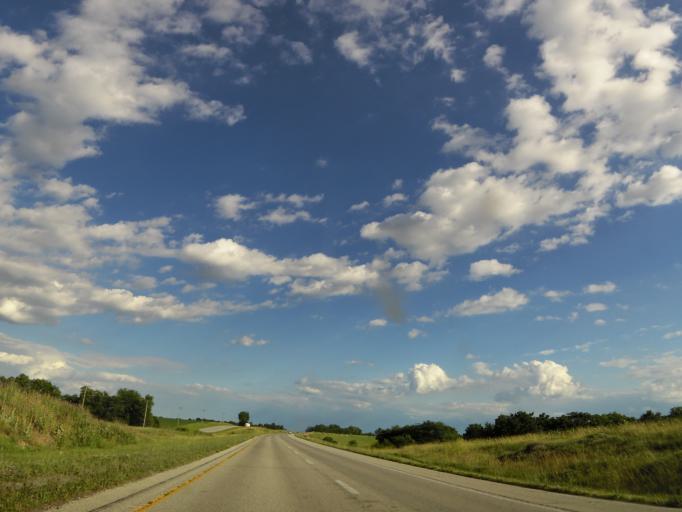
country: US
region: Missouri
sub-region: Lincoln County
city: Troy
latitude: 39.1616
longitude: -90.9762
